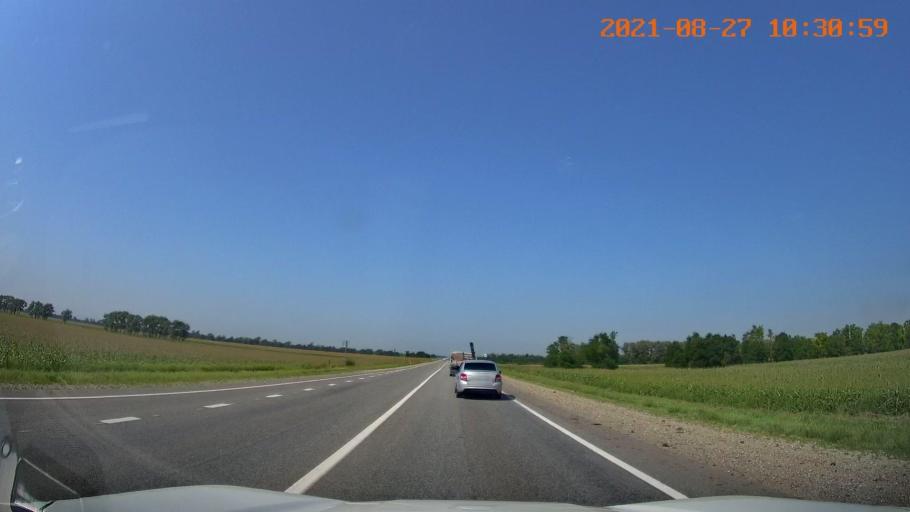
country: RU
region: Karachayevo-Cherkesiya
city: Kavkazskiy
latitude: 44.2627
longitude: 42.1701
